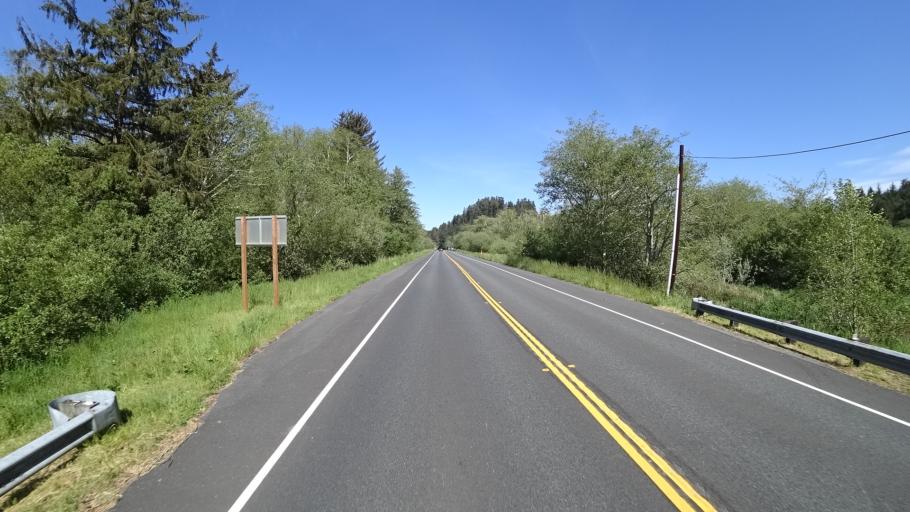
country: US
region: California
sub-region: Del Norte County
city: Bertsch-Oceanview
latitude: 41.5567
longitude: -124.0575
